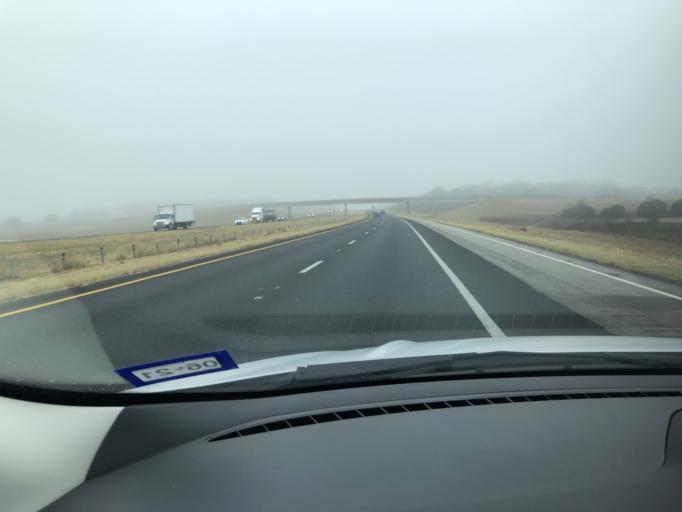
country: US
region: Texas
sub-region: Gonzales County
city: Waelder
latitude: 29.6624
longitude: -97.3861
